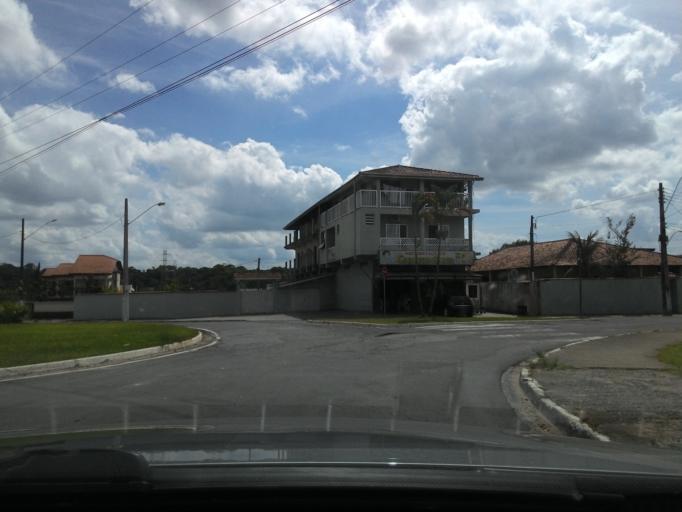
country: BR
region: Sao Paulo
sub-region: Registro
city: Registro
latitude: -24.5052
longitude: -47.8599
